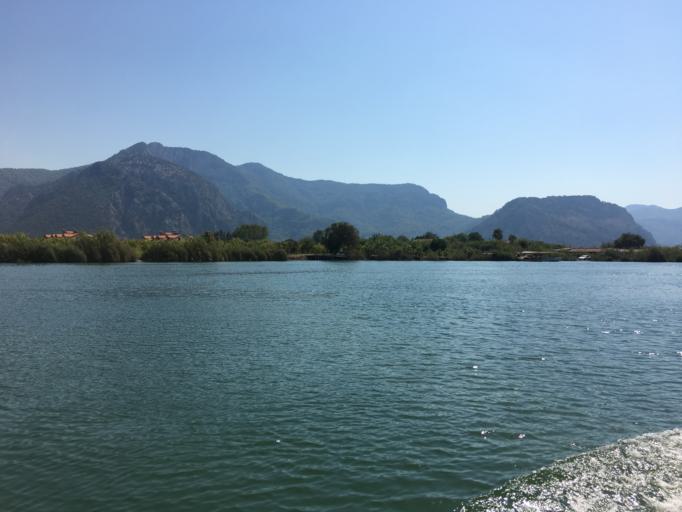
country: TR
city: Dalyan
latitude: 36.8198
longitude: 28.6359
